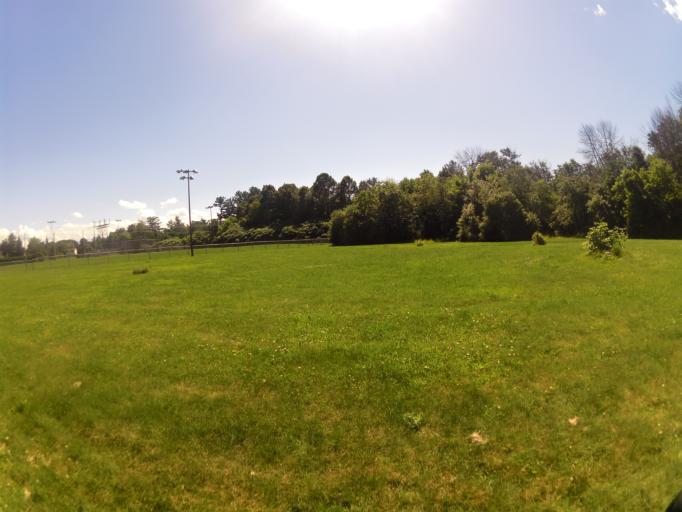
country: CA
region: Ontario
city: Bells Corners
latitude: 45.3278
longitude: -75.7843
